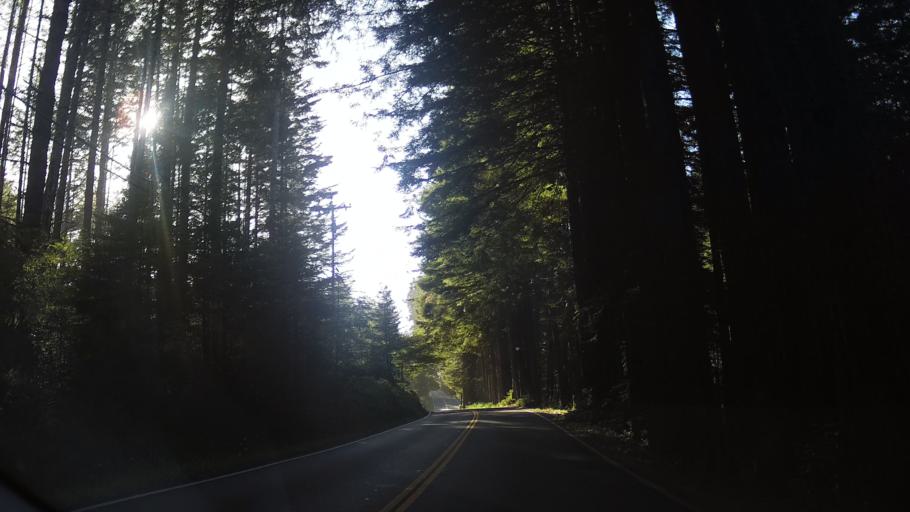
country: US
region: California
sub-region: Mendocino County
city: Fort Bragg
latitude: 39.4058
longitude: -123.7245
